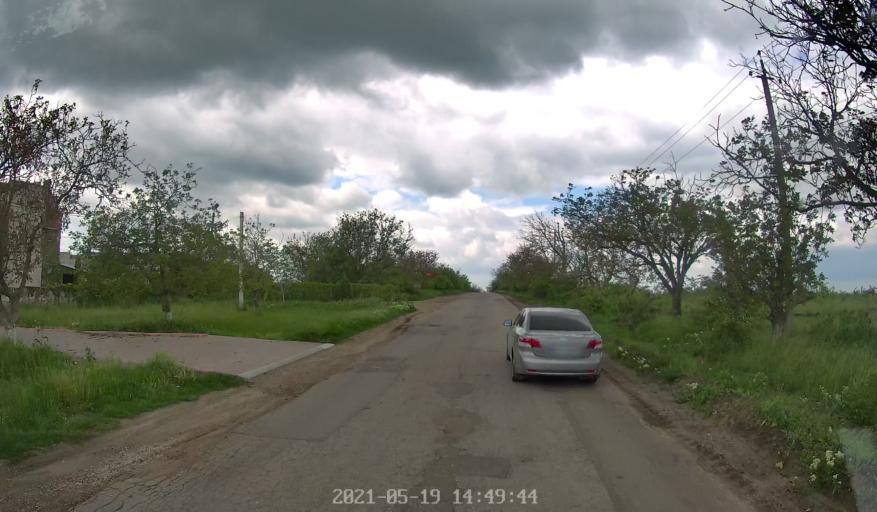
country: MD
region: Chisinau
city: Stauceni
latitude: 47.0521
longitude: 28.9494
